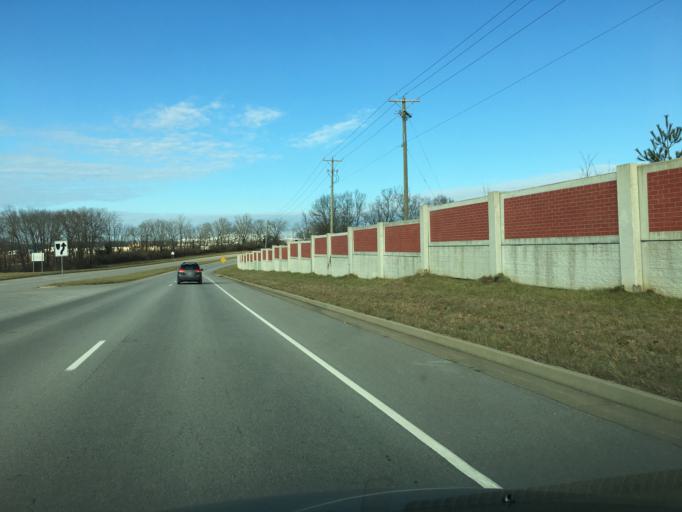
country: US
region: Kentucky
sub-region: Scott County
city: Georgetown
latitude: 38.2126
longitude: -84.5963
